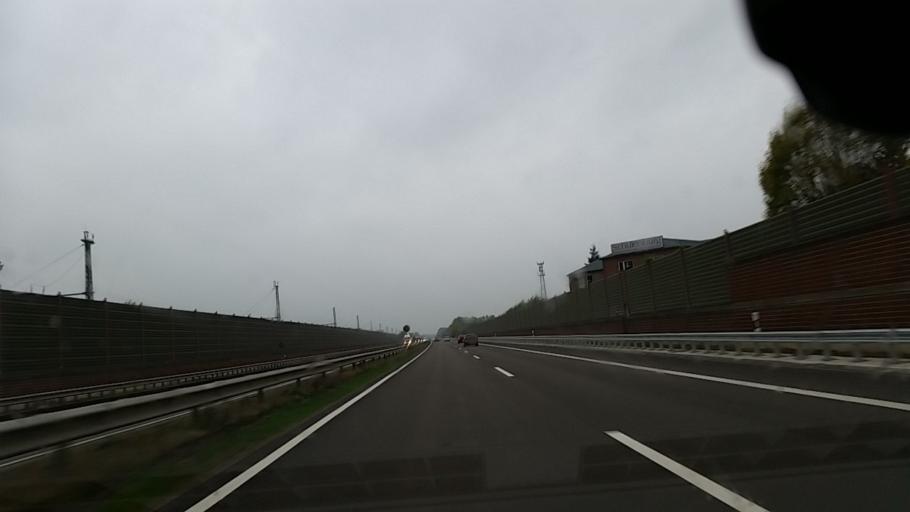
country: DE
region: Lower Saxony
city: Bardowick
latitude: 53.2908
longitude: 10.3723
